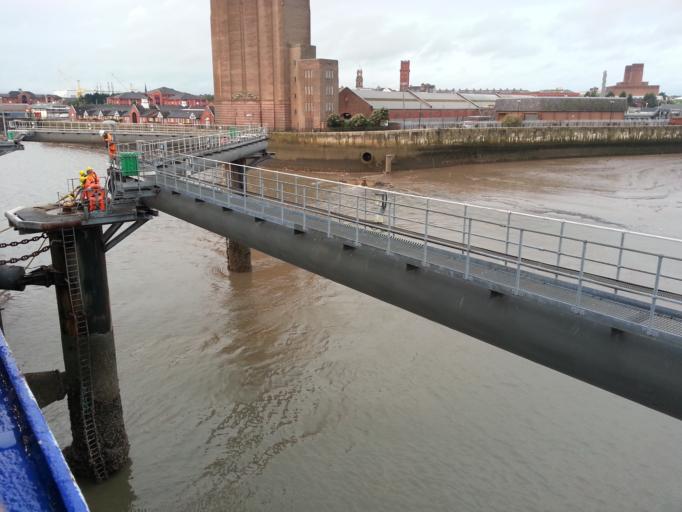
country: GB
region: England
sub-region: Metropolitan Borough of Wirral
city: Birkenhead
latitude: 53.3989
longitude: -3.0097
